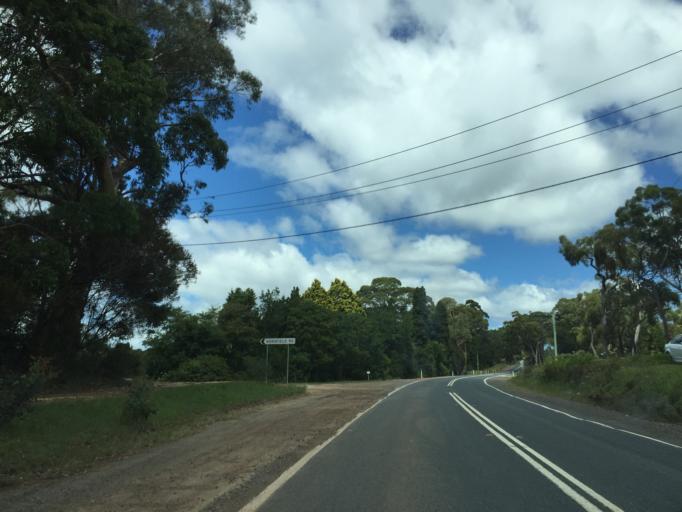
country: AU
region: New South Wales
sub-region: Blue Mountains Municipality
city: Hazelbrook
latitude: -33.5030
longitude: 150.5085
